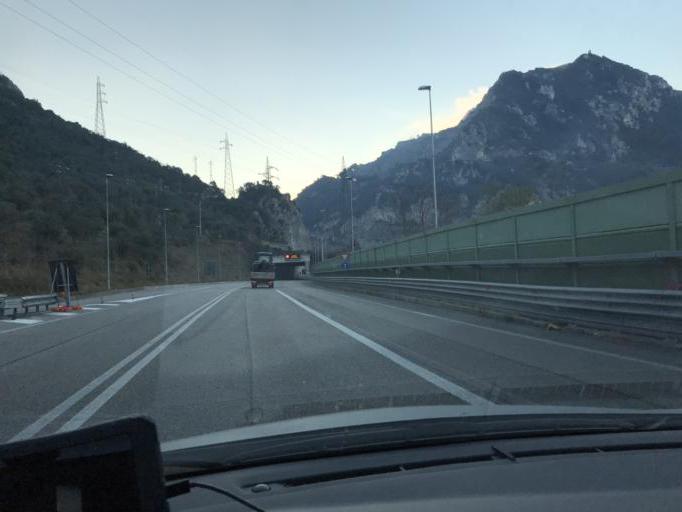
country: IT
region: Umbria
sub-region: Provincia di Terni
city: Terni
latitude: 42.5557
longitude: 12.6956
